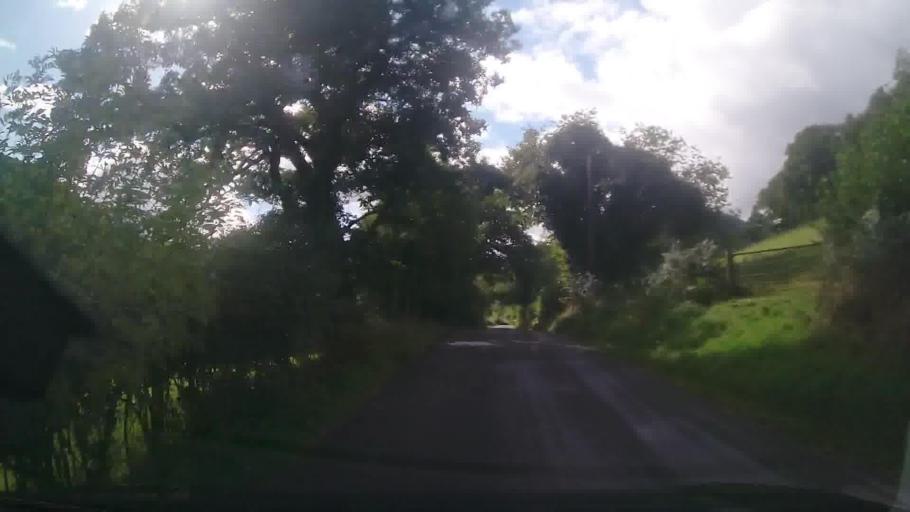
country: GB
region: Wales
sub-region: Gwynedd
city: Bala
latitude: 52.7505
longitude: -3.6367
